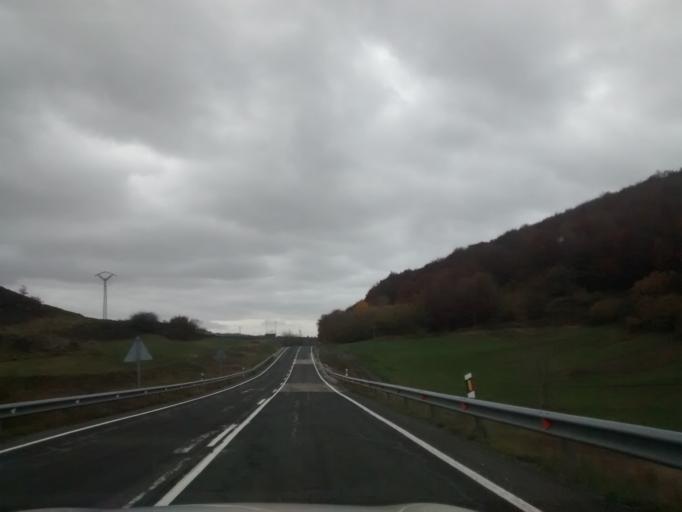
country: ES
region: Cantabria
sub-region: Provincia de Cantabria
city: San Martin de Elines
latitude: 42.9304
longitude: -3.8277
